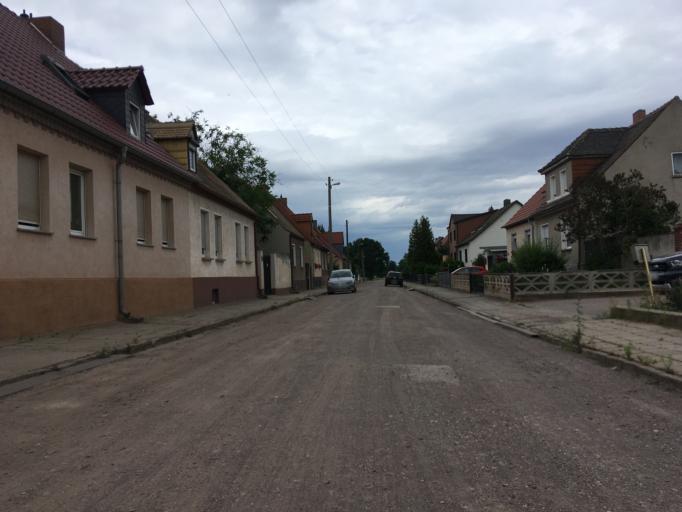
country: DE
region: Saxony-Anhalt
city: Quellendorf
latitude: 51.8115
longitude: 12.1539
